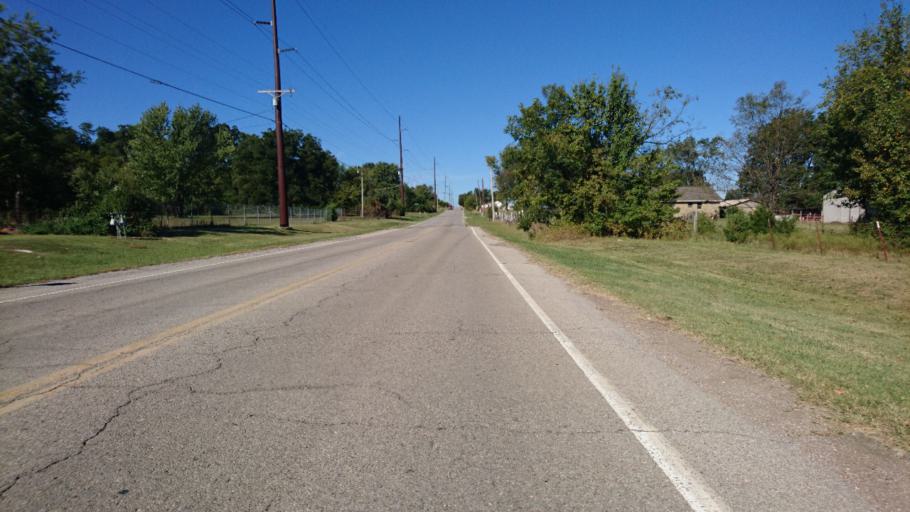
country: US
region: Oklahoma
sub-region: Rogers County
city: Catoosa
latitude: 36.1480
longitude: -95.7871
